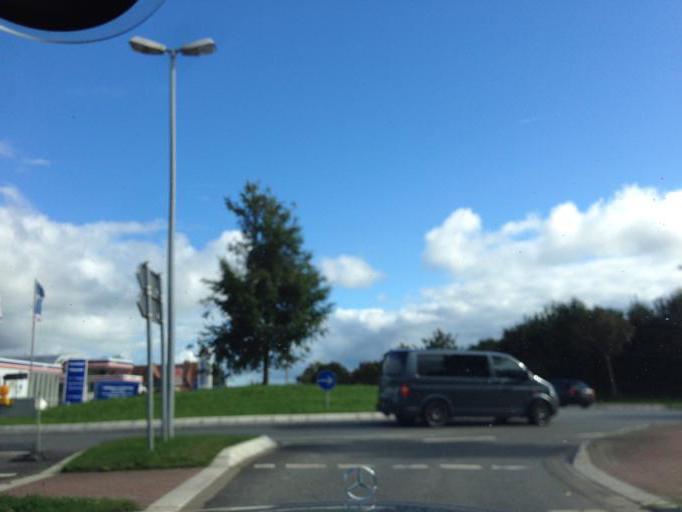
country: DE
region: Schleswig-Holstein
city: Niebull
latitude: 54.7799
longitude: 8.8332
